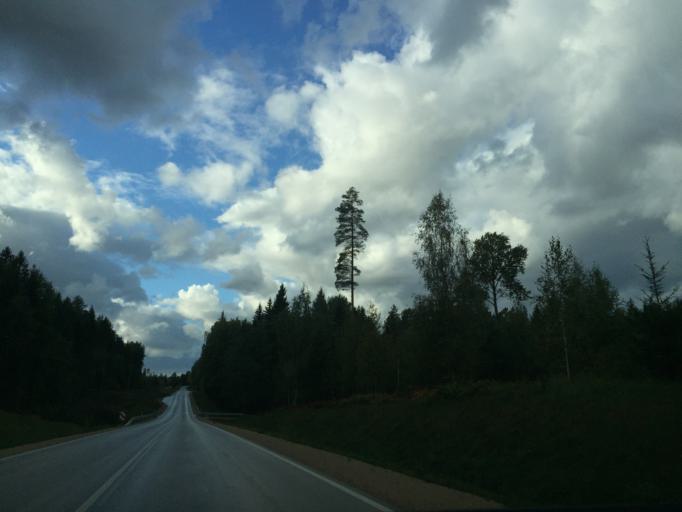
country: LV
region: Ligatne
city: Ligatne
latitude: 57.1583
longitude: 25.0618
